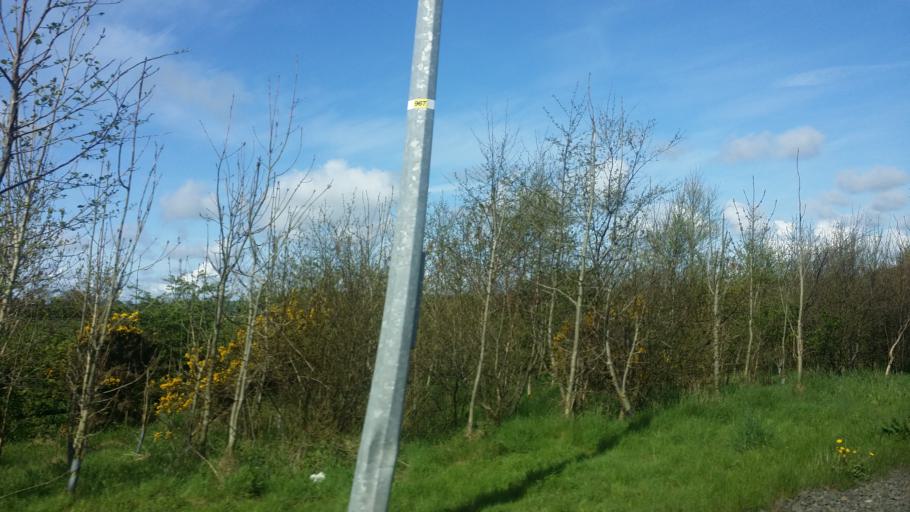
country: IE
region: Leinster
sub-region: An Mhi
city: Kells
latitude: 53.7254
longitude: -6.9477
